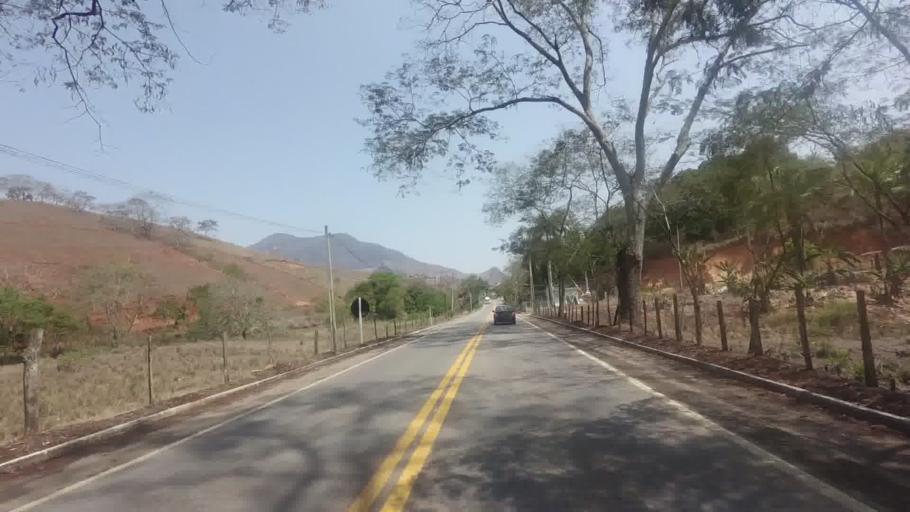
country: BR
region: Espirito Santo
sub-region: Mimoso Do Sul
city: Mimoso do Sul
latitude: -20.9381
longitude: -41.3276
